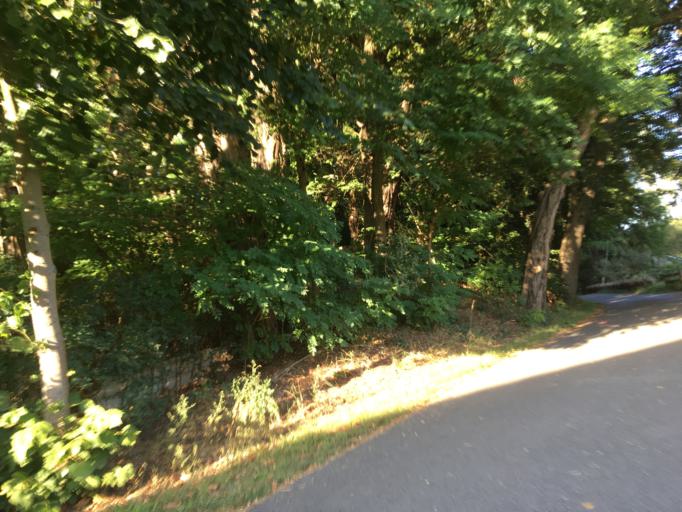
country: DE
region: Saxony
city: Bad Muskau
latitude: 51.5893
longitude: 14.7303
